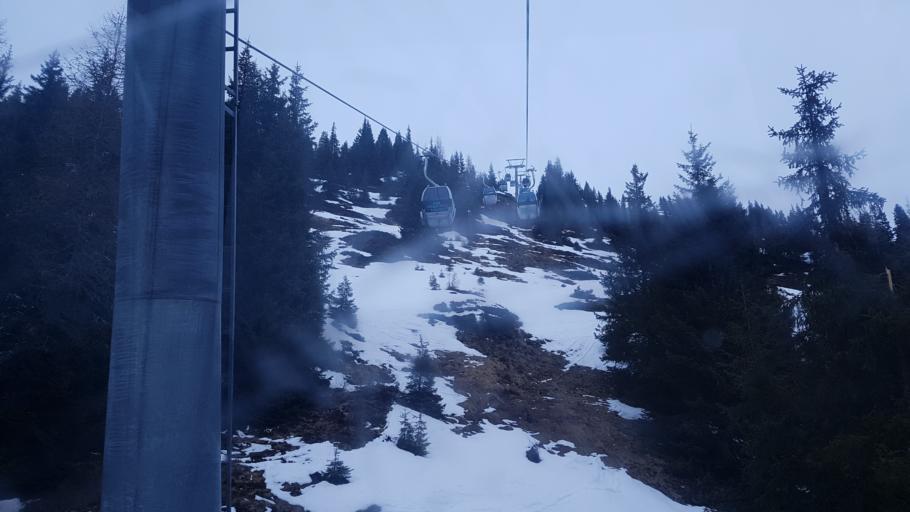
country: AT
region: Salzburg
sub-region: Politischer Bezirk Zell am See
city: Neukirchen am Grossvenediger
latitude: 47.2722
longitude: 12.2812
